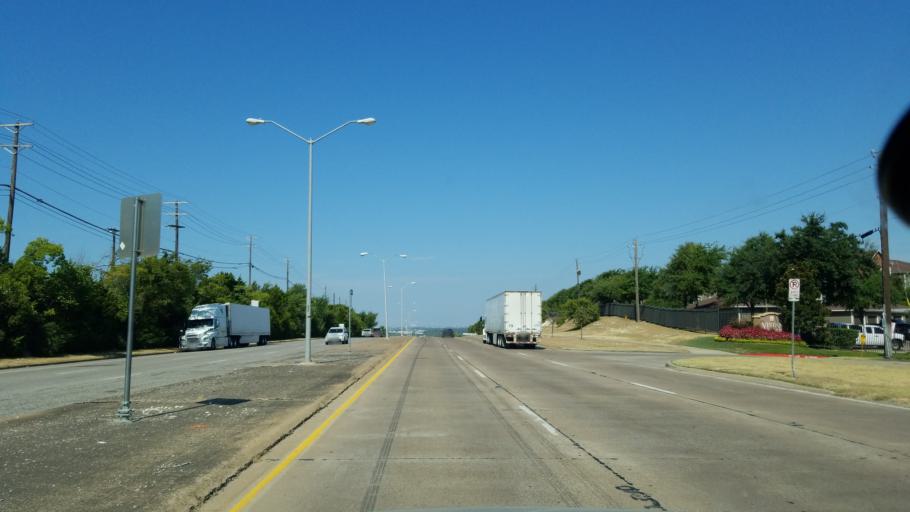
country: US
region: Texas
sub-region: Dallas County
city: Cockrell Hill
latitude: 32.7497
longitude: -96.8980
